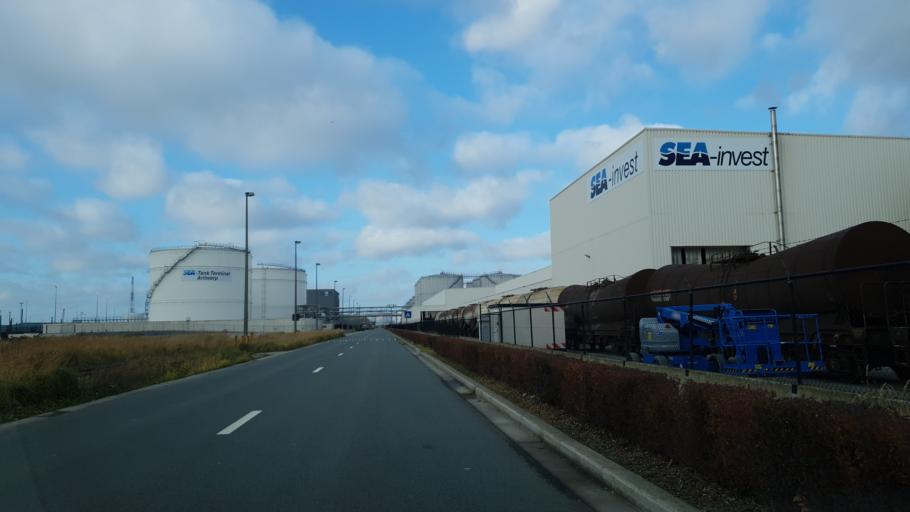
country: BE
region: Flanders
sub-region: Provincie Antwerpen
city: Zwijndrecht
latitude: 51.2664
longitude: 4.3617
